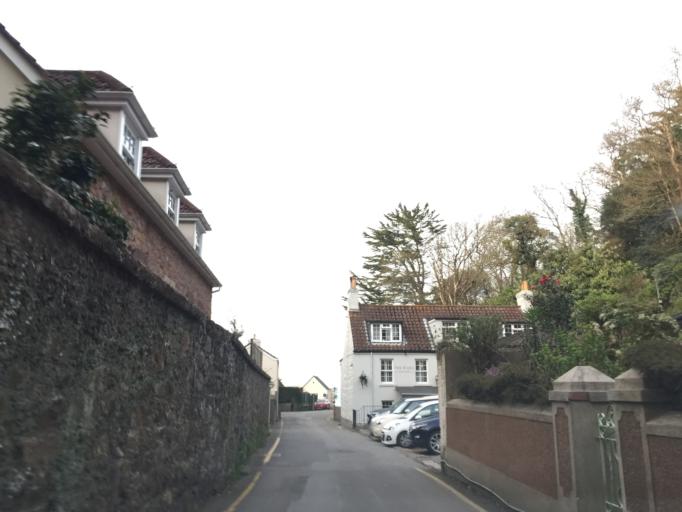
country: JE
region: St Helier
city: Saint Helier
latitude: 49.2350
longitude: -2.0465
